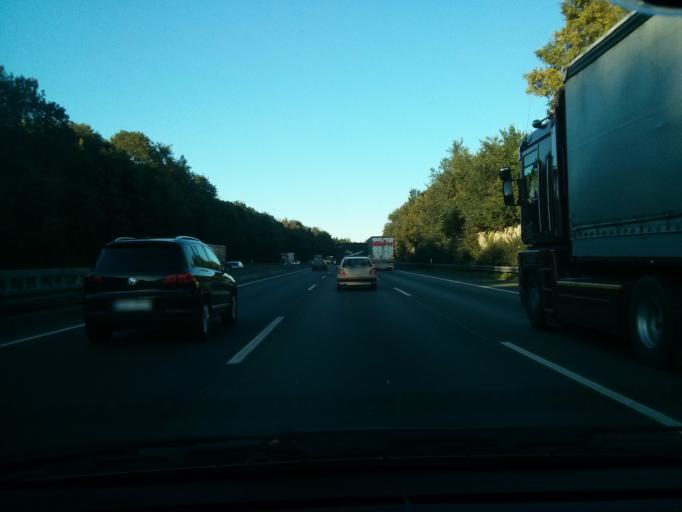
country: DE
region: North Rhine-Westphalia
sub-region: Regierungsbezirk Arnsberg
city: Holzwickede
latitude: 51.4745
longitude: 7.6037
